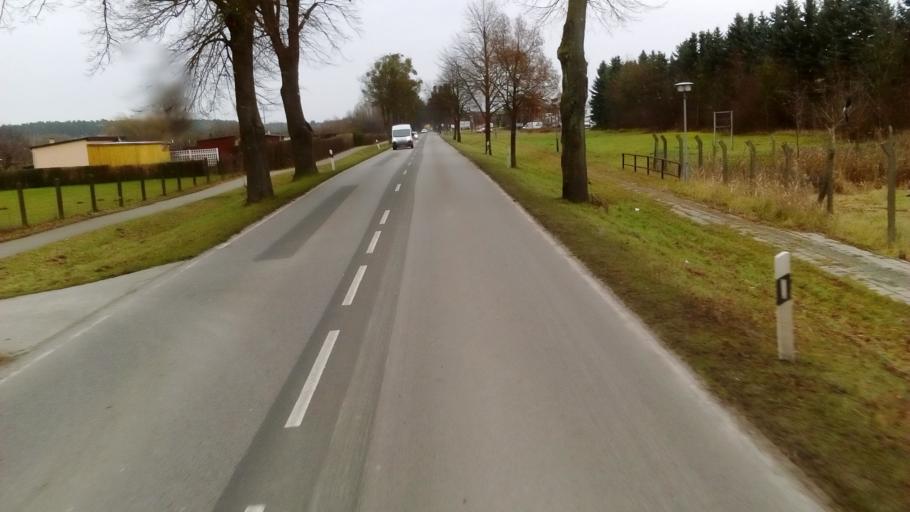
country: DE
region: Mecklenburg-Vorpommern
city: Neustrelitz
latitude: 53.3445
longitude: 13.0864
